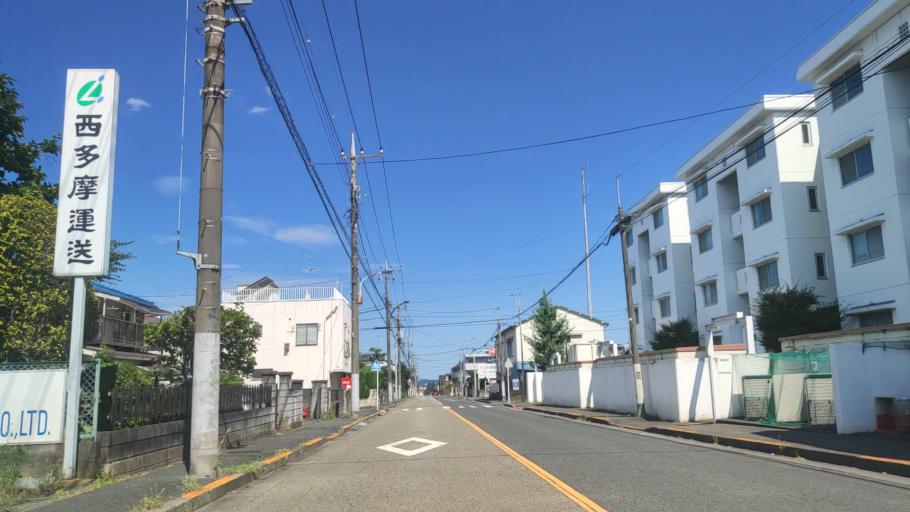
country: JP
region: Tokyo
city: Hachioji
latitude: 35.6501
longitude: 139.3253
